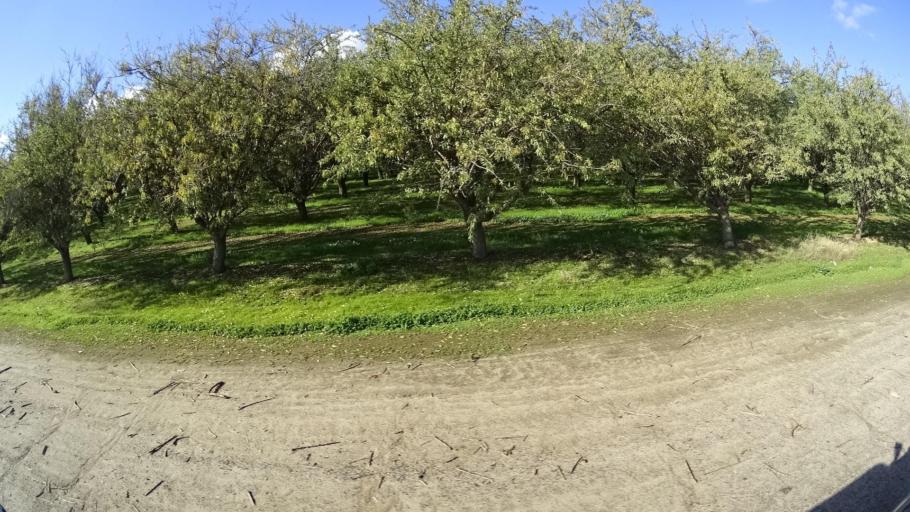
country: US
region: California
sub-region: Kern County
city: McFarland
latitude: 35.6789
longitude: -119.2587
